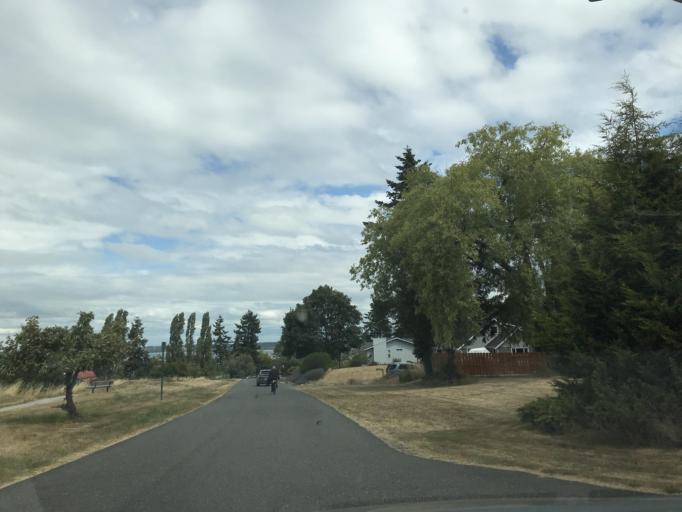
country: US
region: Washington
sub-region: Whatcom County
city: Bellingham
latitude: 48.7168
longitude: -122.5115
